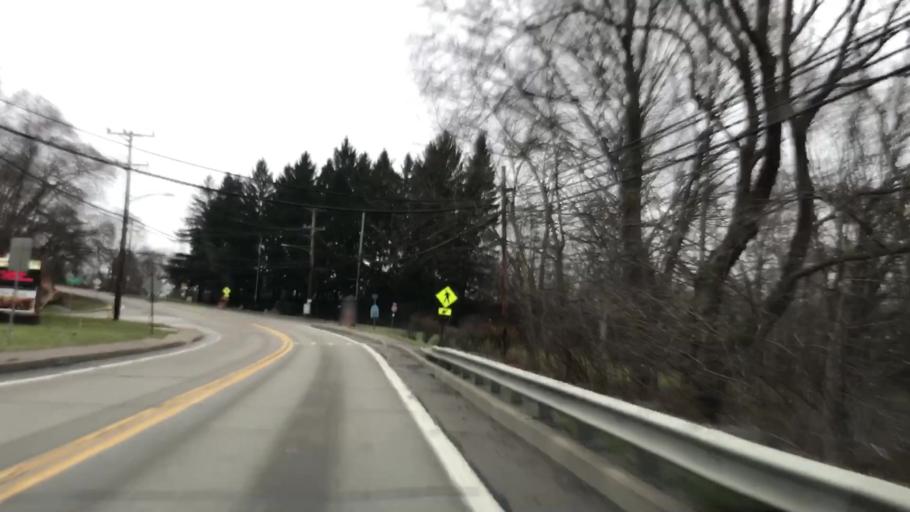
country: US
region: Pennsylvania
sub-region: Allegheny County
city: Leetsdale
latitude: 40.5559
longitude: -80.2199
